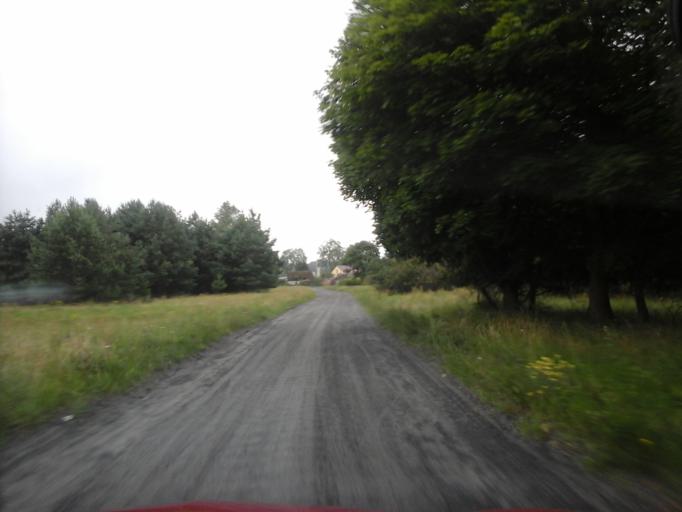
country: PL
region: Lubusz
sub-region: Powiat strzelecko-drezdenecki
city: Dobiegniew
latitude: 53.0758
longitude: 15.7814
